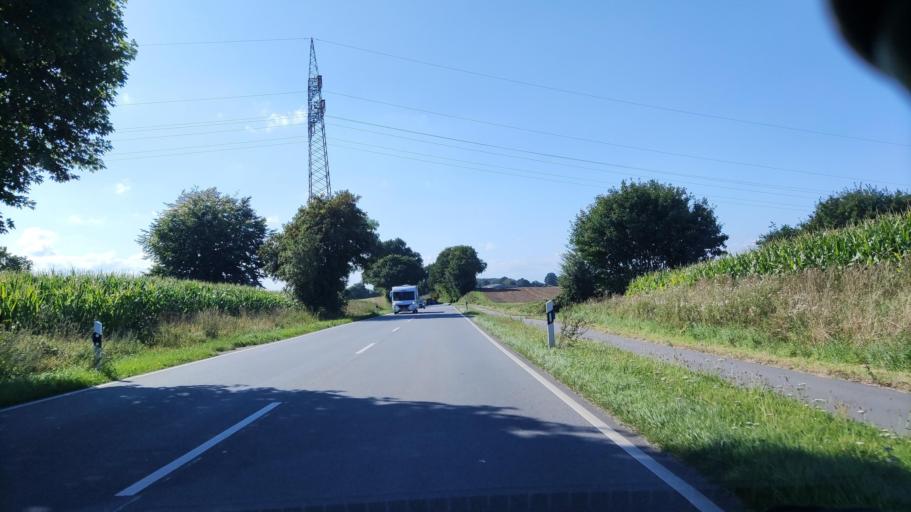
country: DE
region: Schleswig-Holstein
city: Osterby
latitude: 54.4584
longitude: 9.7757
